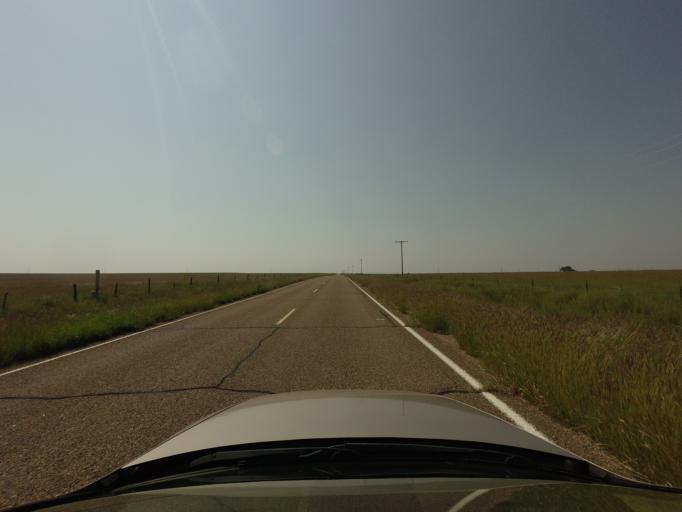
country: US
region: New Mexico
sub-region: Curry County
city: Cannon Air Force Base
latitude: 34.6802
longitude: -103.6355
